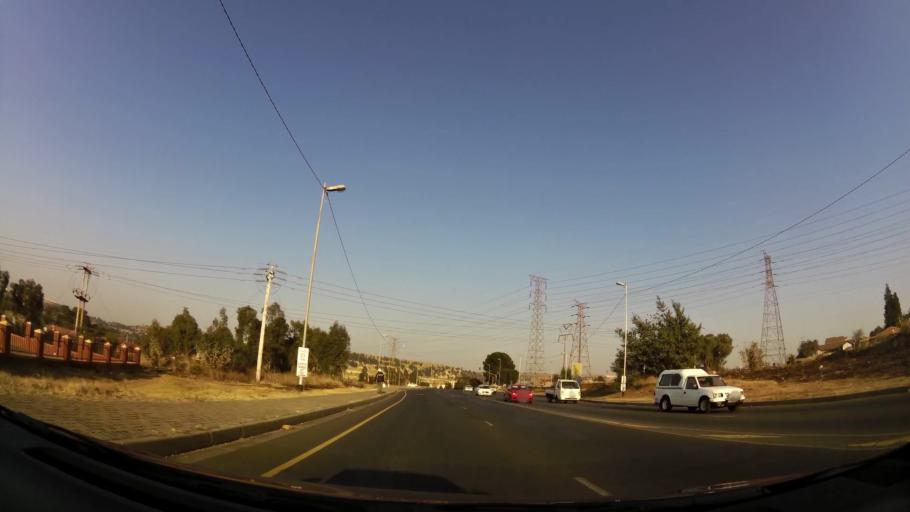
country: ZA
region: Gauteng
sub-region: City of Johannesburg Metropolitan Municipality
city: Johannesburg
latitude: -26.2157
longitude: 27.9847
